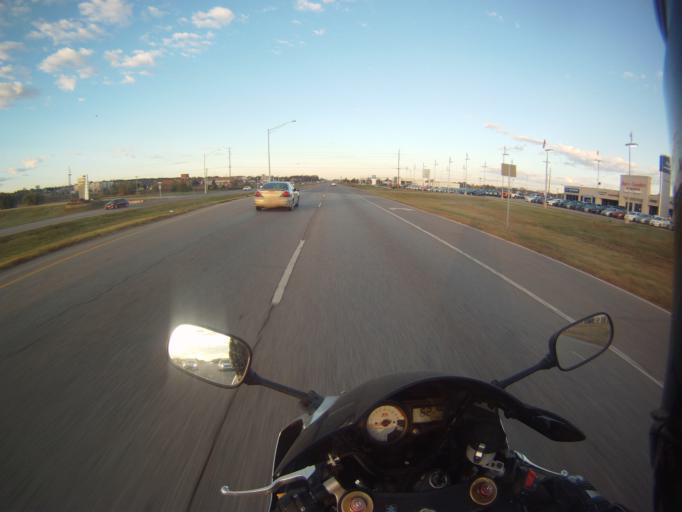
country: US
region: Oklahoma
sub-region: Payne County
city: Stillwater
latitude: 36.1164
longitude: -97.1122
